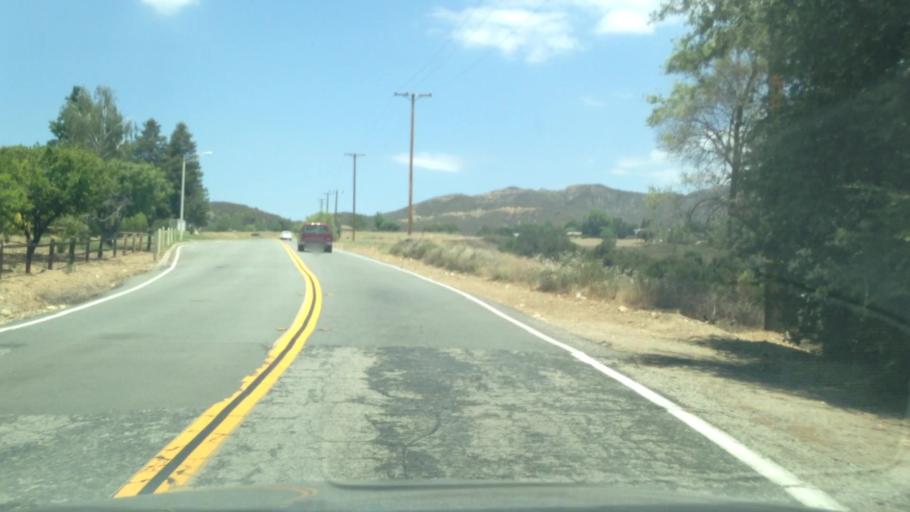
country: US
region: California
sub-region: Riverside County
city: Cherry Valley
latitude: 34.0047
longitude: -116.9633
